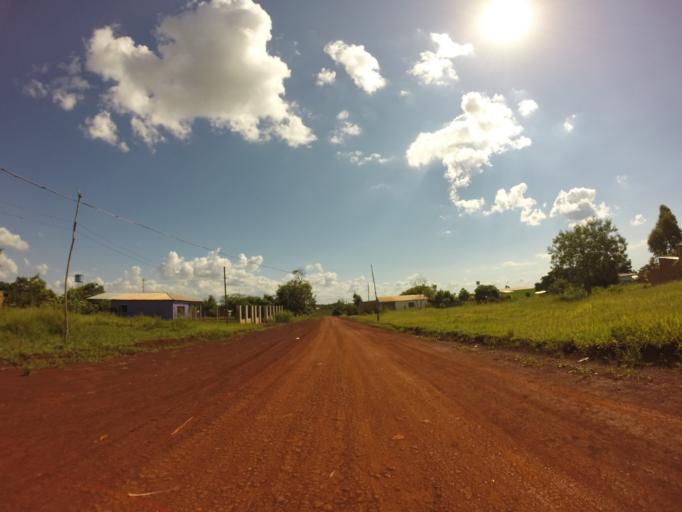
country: PY
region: Alto Parana
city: Ciudad del Este
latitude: -25.3768
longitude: -54.6603
